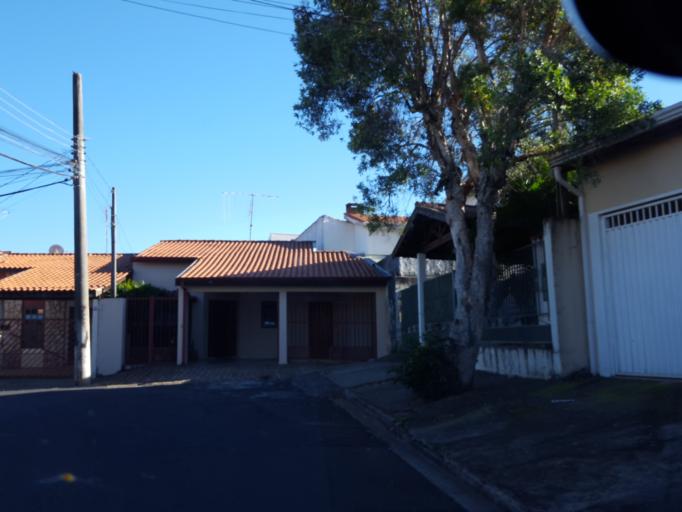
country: BR
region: Sao Paulo
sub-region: Indaiatuba
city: Indaiatuba
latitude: -23.0739
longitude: -47.1999
